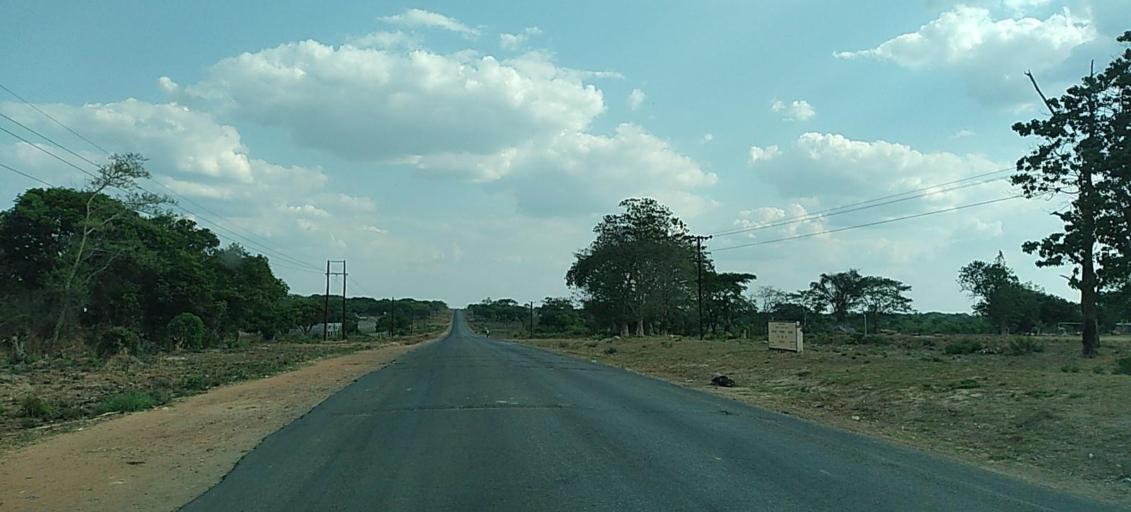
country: ZM
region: Copperbelt
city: Luanshya
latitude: -13.2624
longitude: 28.4065
